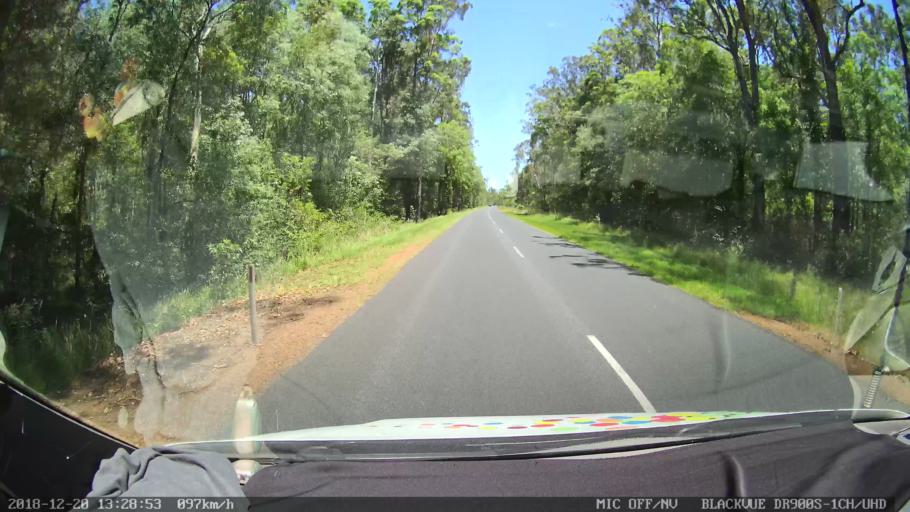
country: AU
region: New South Wales
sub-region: Clarence Valley
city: Gordon
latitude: -29.1810
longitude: 152.9893
